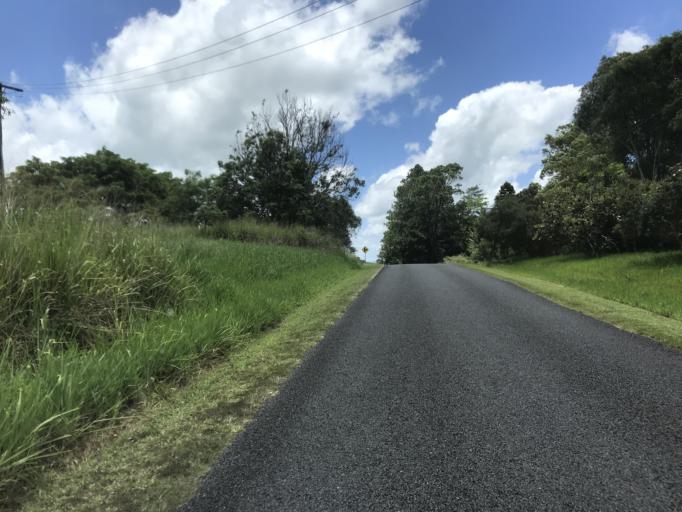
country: AU
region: Queensland
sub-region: Tablelands
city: Atherton
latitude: -17.3381
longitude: 145.5817
